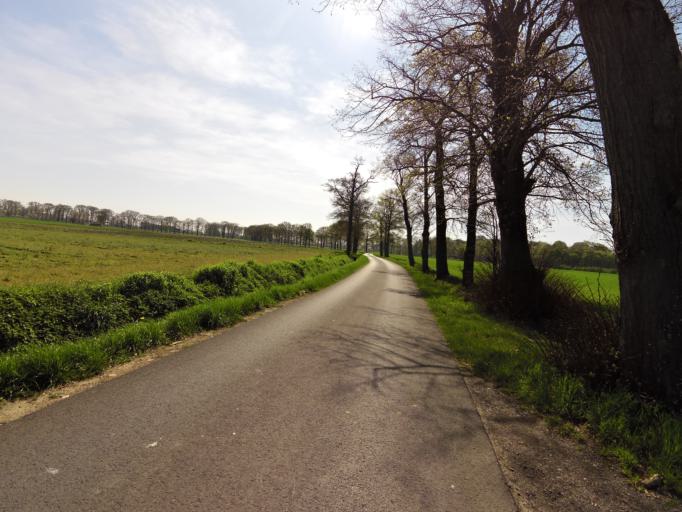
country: BE
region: Flanders
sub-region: Provincie West-Vlaanderen
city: Ichtegem
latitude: 51.1144
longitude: 3.0030
